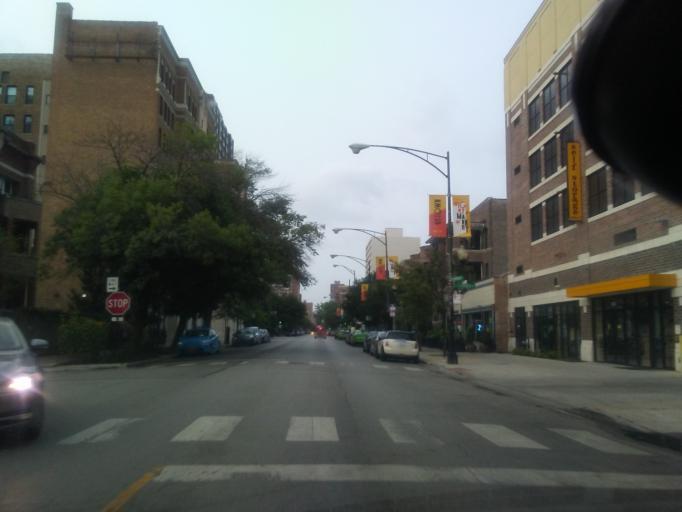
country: US
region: Illinois
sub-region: Cook County
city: Evanston
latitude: 41.9744
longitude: -87.6550
